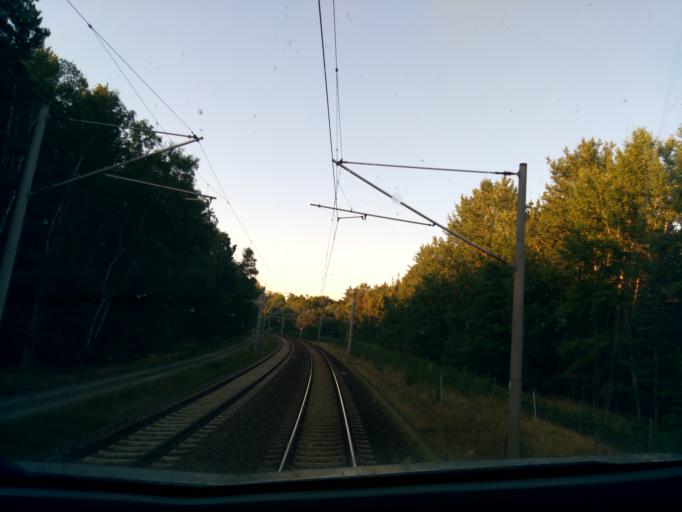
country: DE
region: Brandenburg
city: Bestensee
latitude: 52.2137
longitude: 13.6176
